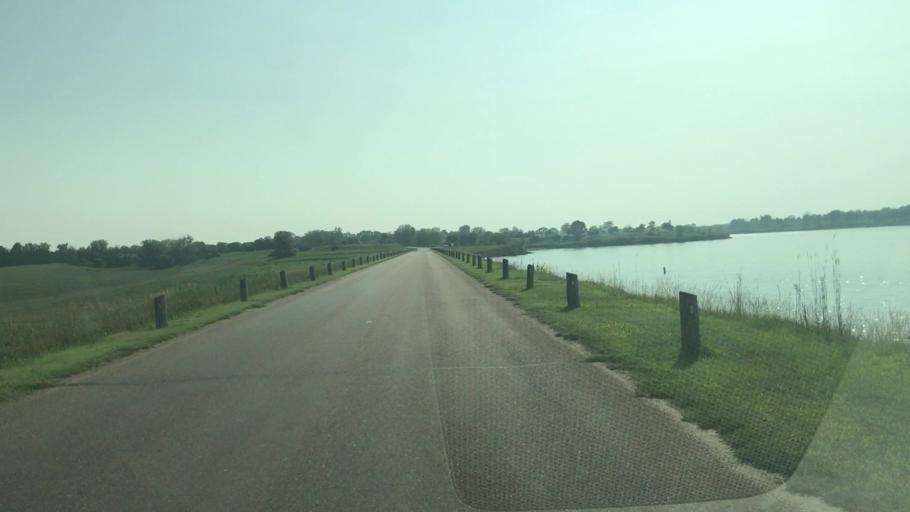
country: US
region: Nebraska
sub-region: Sherman County
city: Loup City
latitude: 41.3013
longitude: -98.8850
